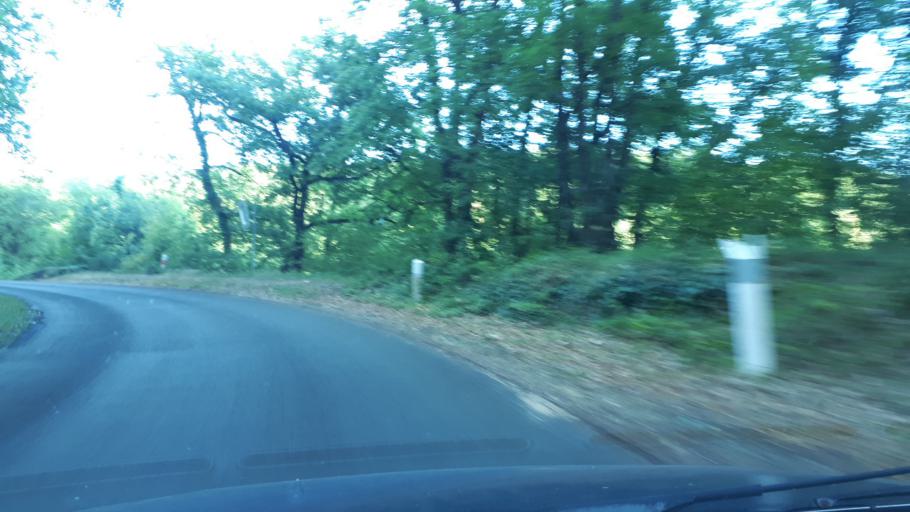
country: FR
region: Centre
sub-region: Departement du Loir-et-Cher
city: Villiers-sur-Loir
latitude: 47.7691
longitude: 0.9577
